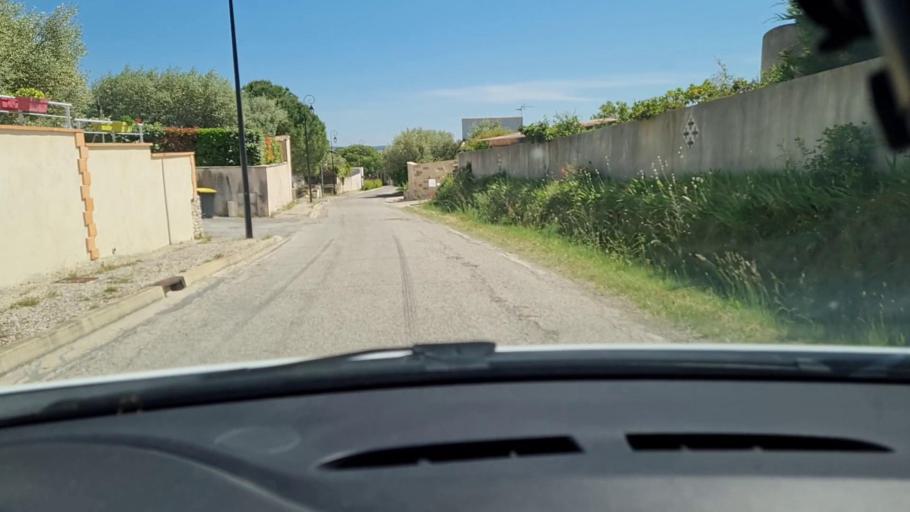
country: FR
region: Languedoc-Roussillon
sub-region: Departement du Gard
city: Clarensac
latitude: 43.8309
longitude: 4.2012
